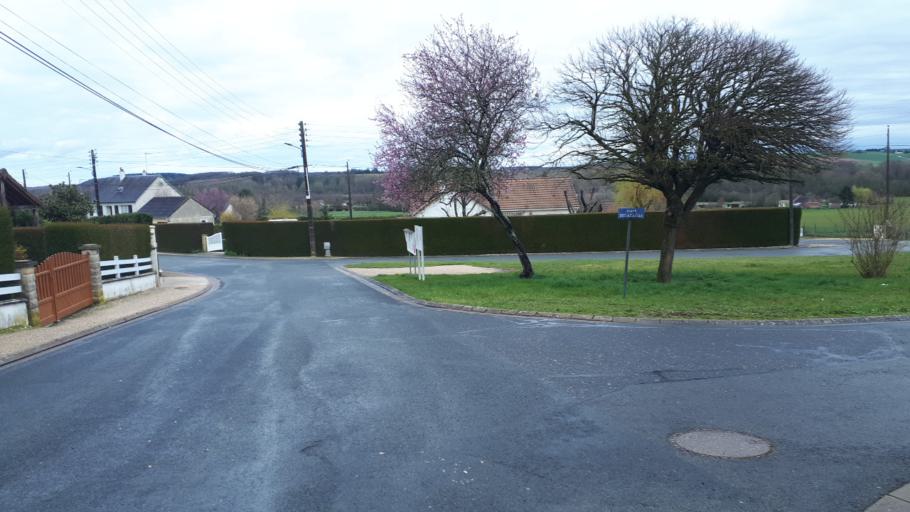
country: FR
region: Centre
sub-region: Departement du Loir-et-Cher
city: Moree
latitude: 47.9224
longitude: 1.1981
